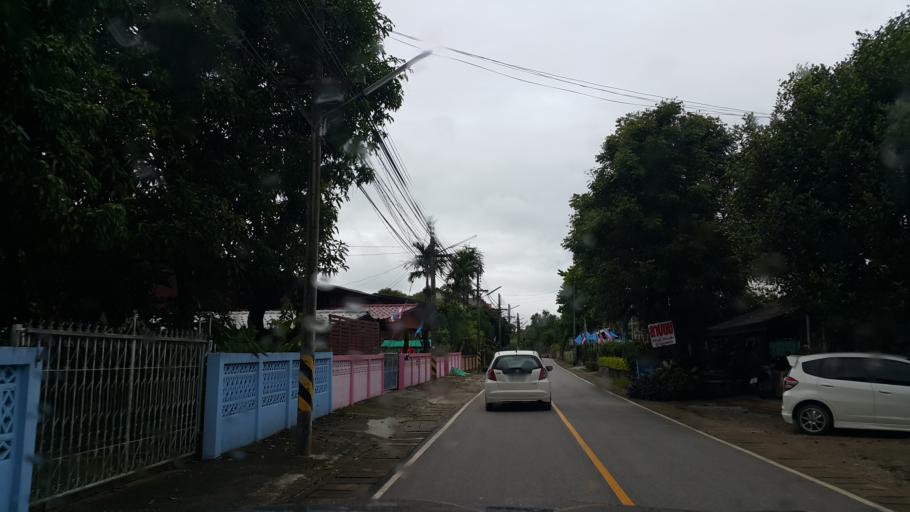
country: TH
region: Phayao
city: Chiang Kham
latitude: 19.5320
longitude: 100.2958
